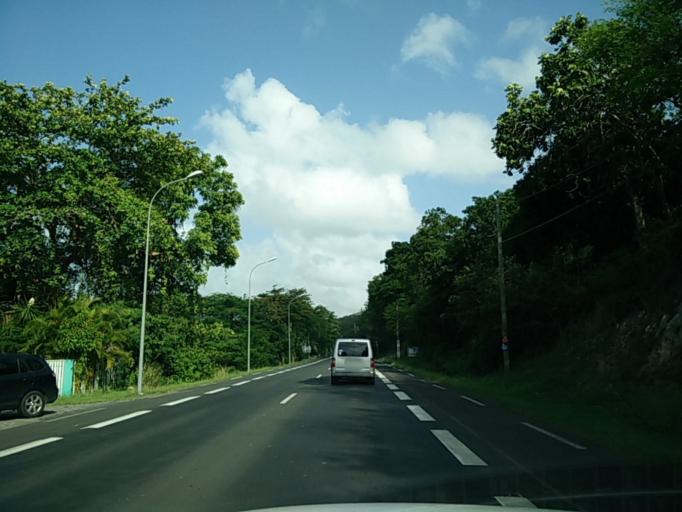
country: GP
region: Guadeloupe
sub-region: Guadeloupe
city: Le Gosier
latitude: 16.2172
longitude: -61.4835
